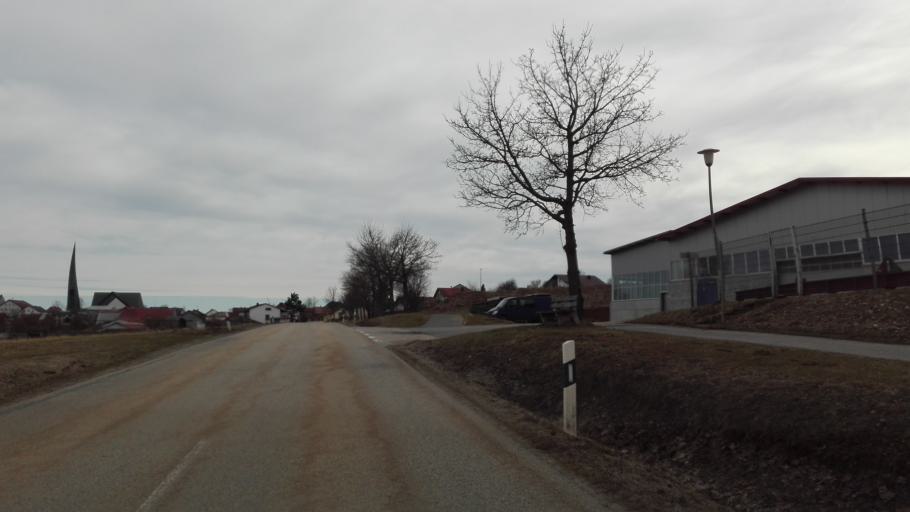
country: DE
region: Bavaria
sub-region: Lower Bavaria
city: Wegscheid
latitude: 48.6064
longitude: 13.7840
